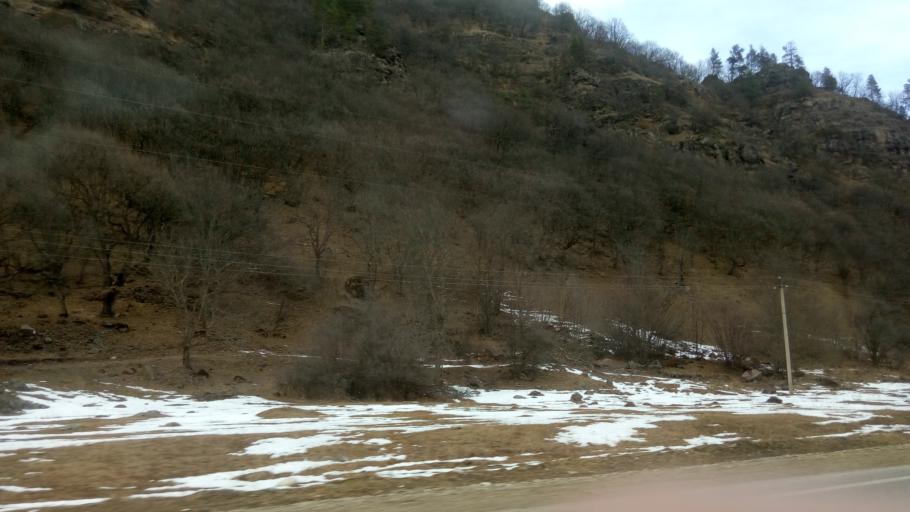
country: RU
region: Karachayevo-Cherkesiya
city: Karachayevsk
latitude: 43.5955
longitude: 41.8600
